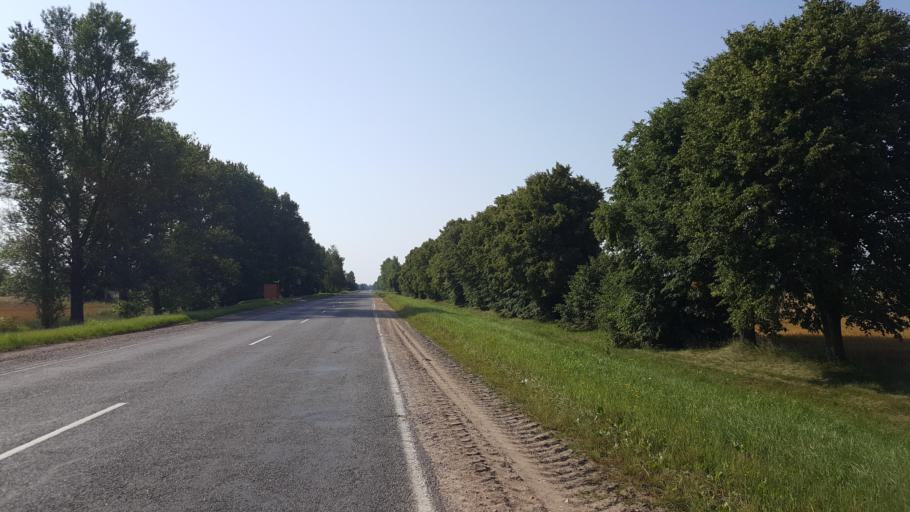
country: BY
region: Brest
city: Kamyanyets
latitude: 52.3596
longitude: 23.8926
